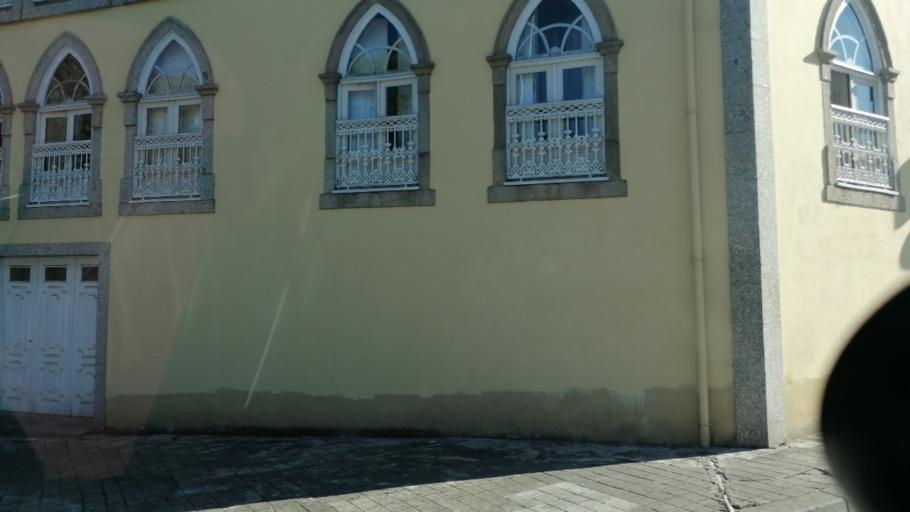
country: PT
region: Porto
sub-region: Santo Tirso
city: Santo Tirso
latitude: 41.3462
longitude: -8.4738
